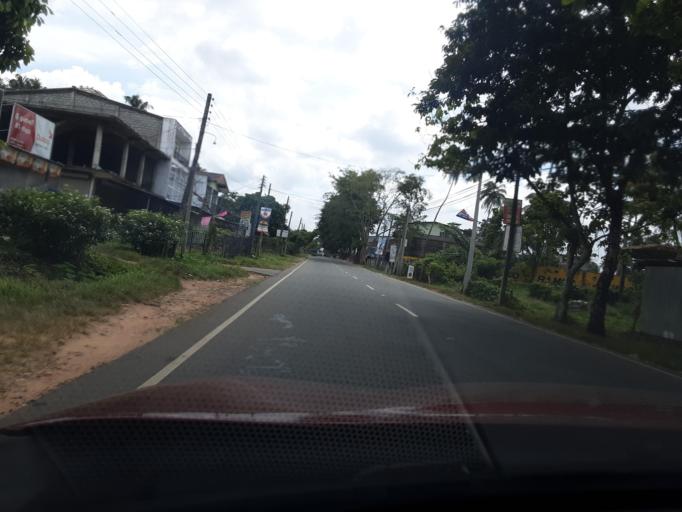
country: LK
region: North Western
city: Kuliyapitiya
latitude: 7.4517
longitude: 80.1664
